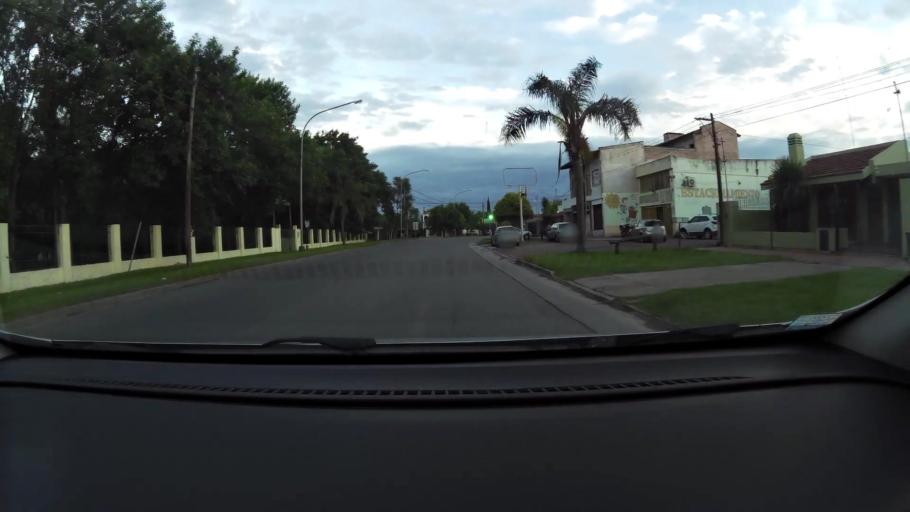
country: AR
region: Buenos Aires
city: San Nicolas de los Arroyos
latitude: -33.3143
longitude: -60.2345
